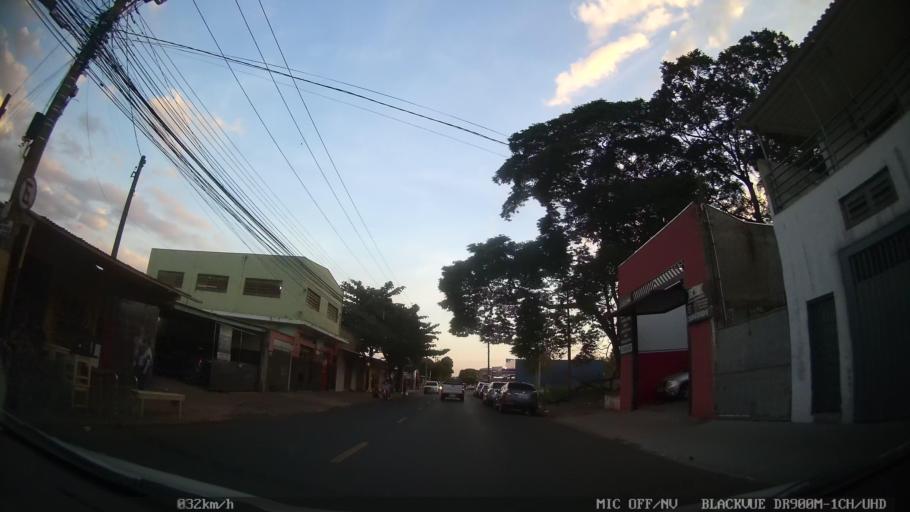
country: BR
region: Sao Paulo
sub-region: Ribeirao Preto
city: Ribeirao Preto
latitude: -21.1300
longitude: -47.8130
